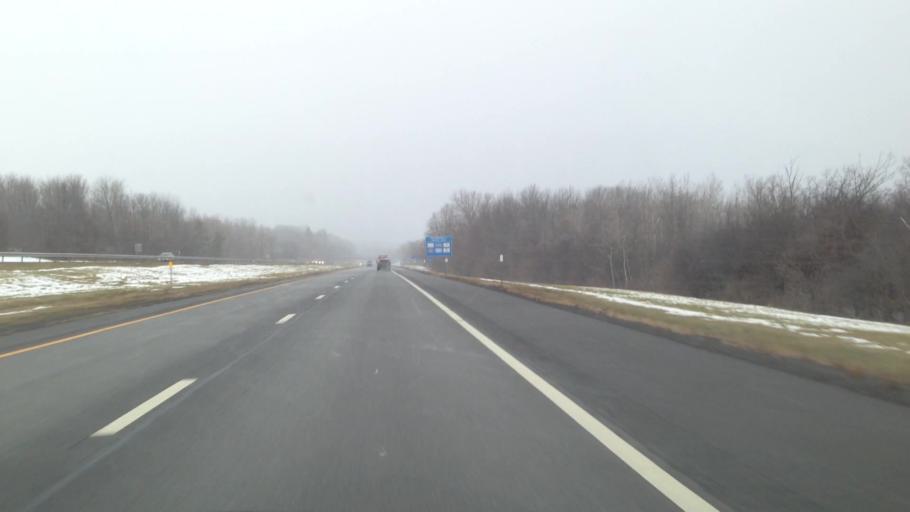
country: US
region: New York
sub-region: Schenectady County
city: Scotia
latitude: 42.8806
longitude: -74.0681
